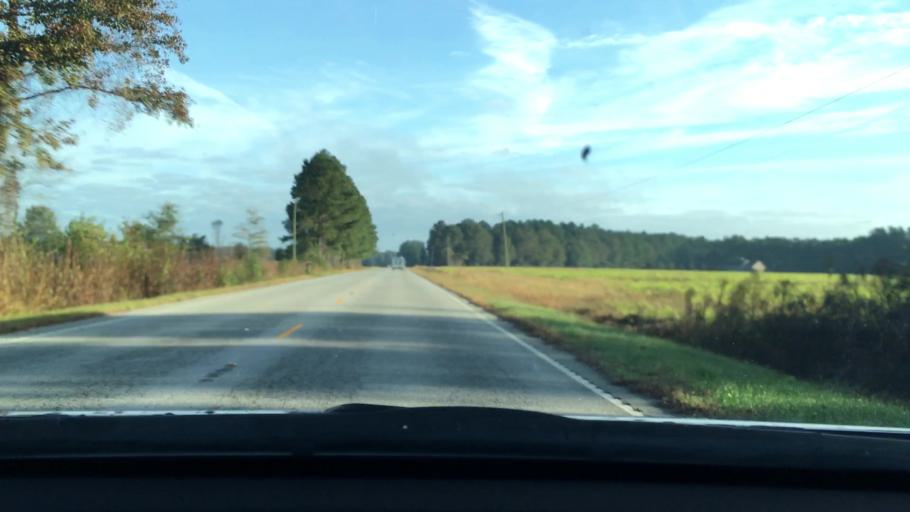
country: US
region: South Carolina
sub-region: Sumter County
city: East Sumter
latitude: 34.0235
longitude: -80.2773
